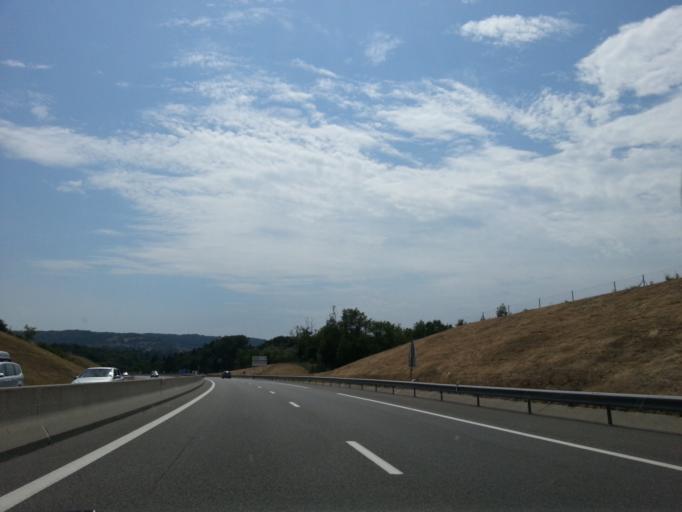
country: FR
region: Rhone-Alpes
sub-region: Departement de la Haute-Savoie
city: Feigeres
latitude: 46.1224
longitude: 6.0880
